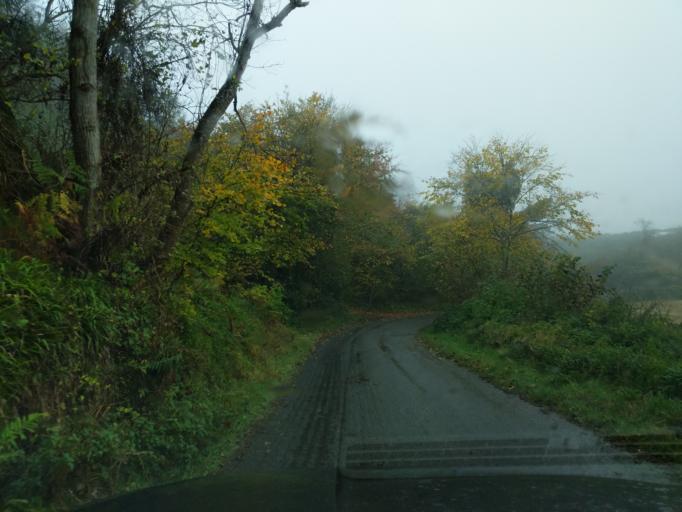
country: GB
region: Scotland
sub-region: East Lothian
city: Dunbar
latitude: 55.9436
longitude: -2.4243
